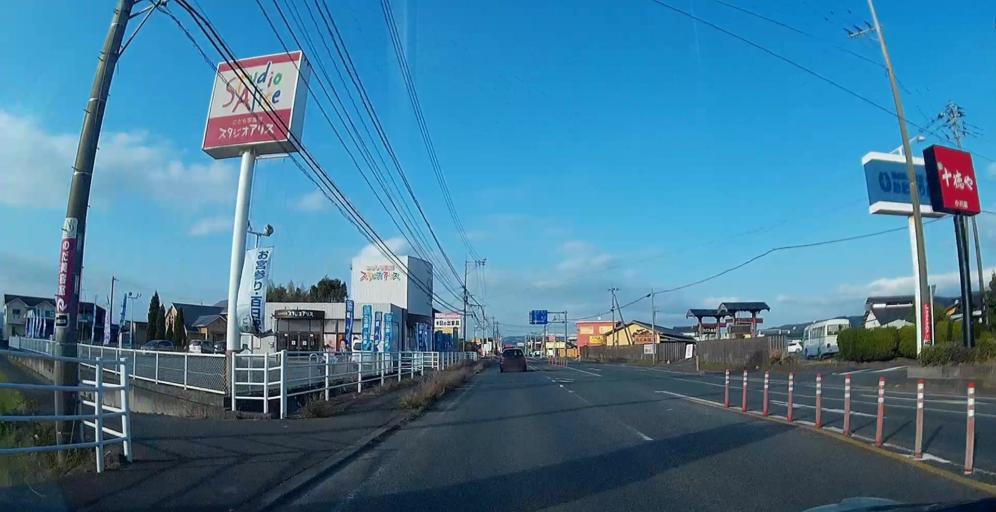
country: JP
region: Kumamoto
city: Matsubase
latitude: 32.5987
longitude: 130.7023
